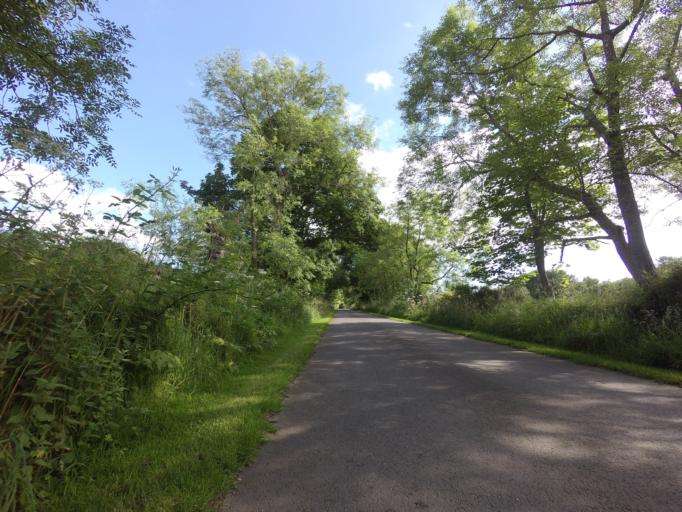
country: GB
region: Scotland
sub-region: Aberdeenshire
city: Turriff
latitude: 57.5921
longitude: -2.5068
